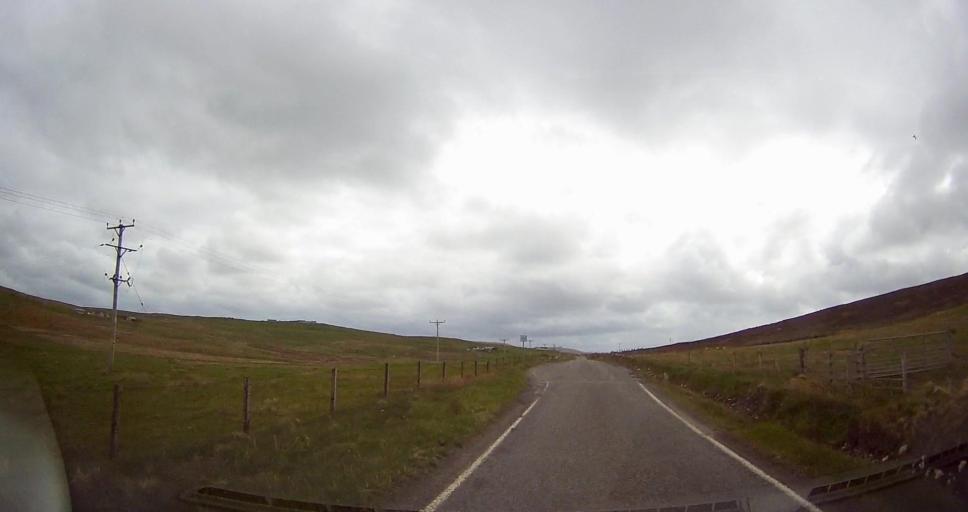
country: GB
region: Scotland
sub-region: Shetland Islands
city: Sandwick
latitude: 60.2485
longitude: -1.5087
